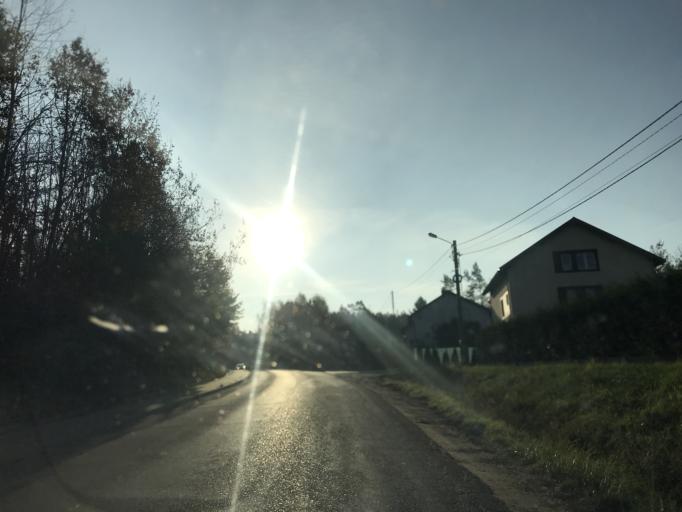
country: PL
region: Pomeranian Voivodeship
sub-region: Powiat pucki
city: Krokowa
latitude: 54.7990
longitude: 18.1107
